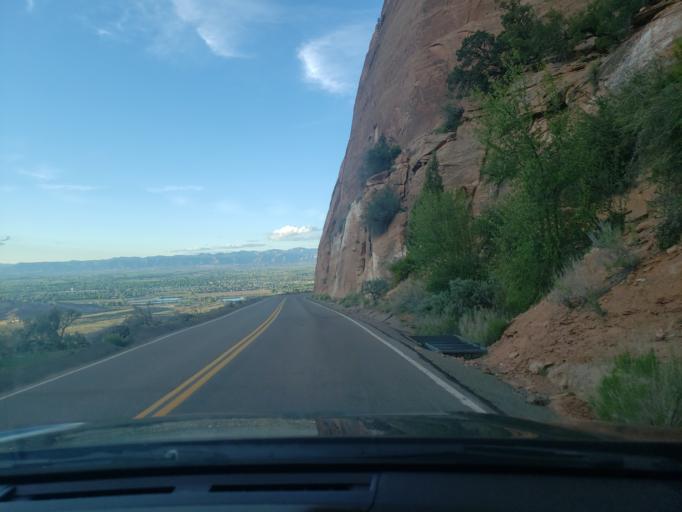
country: US
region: Colorado
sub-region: Mesa County
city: Fruita
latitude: 39.1138
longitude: -108.7307
